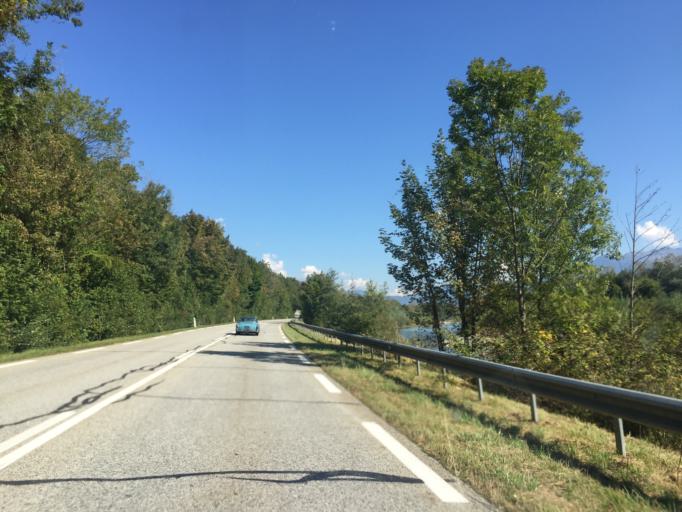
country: FR
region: Rhone-Alpes
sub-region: Departement de la Savoie
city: Gresy-sur-Isere
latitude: 45.6037
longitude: 6.2798
